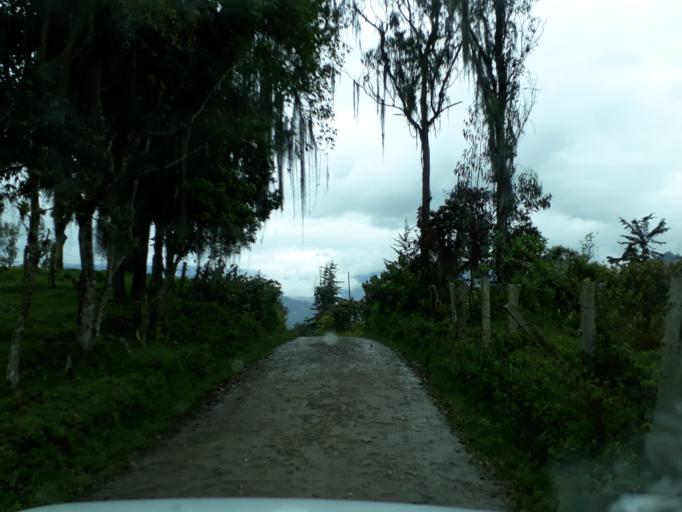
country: CO
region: Cundinamarca
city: Gacheta
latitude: 4.8616
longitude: -73.6356
